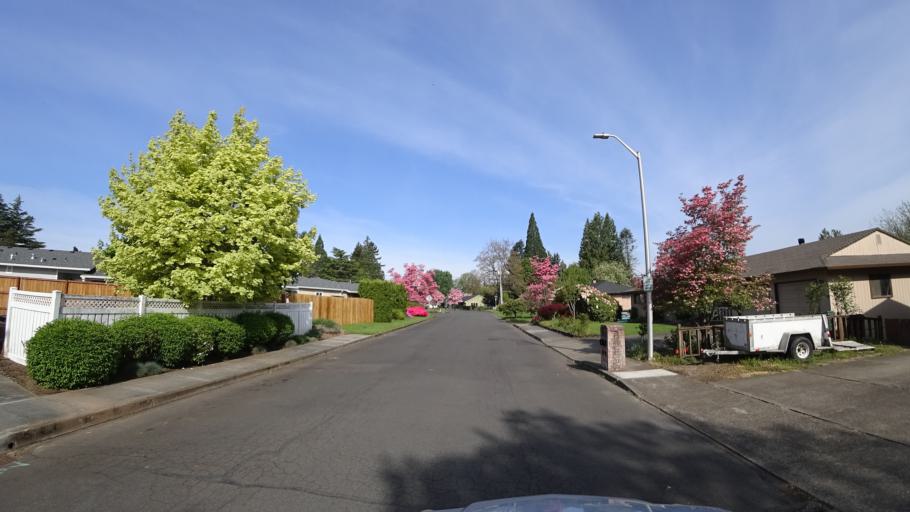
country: US
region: Oregon
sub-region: Washington County
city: Hillsboro
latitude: 45.5226
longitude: -122.9669
